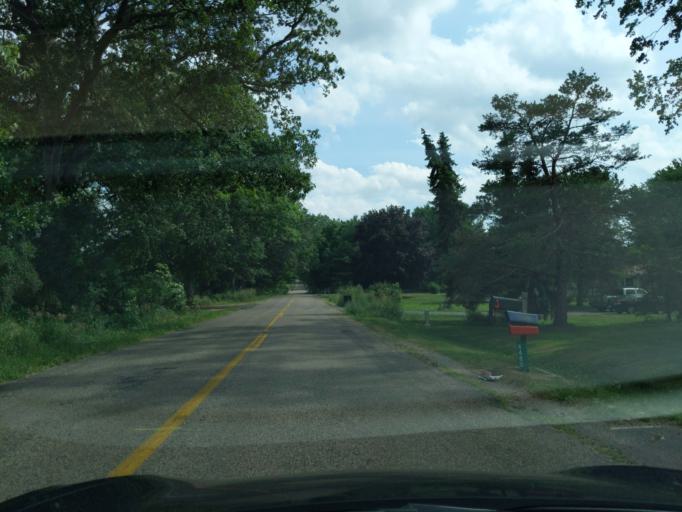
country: US
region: Michigan
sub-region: Eaton County
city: Eaton Rapids
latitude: 42.5024
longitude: -84.6307
